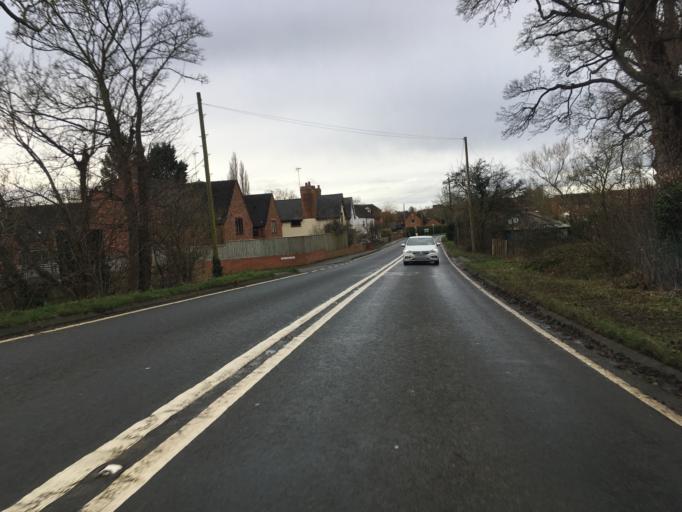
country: GB
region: England
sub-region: Worcestershire
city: Evesham
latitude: 52.0489
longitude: -1.9643
